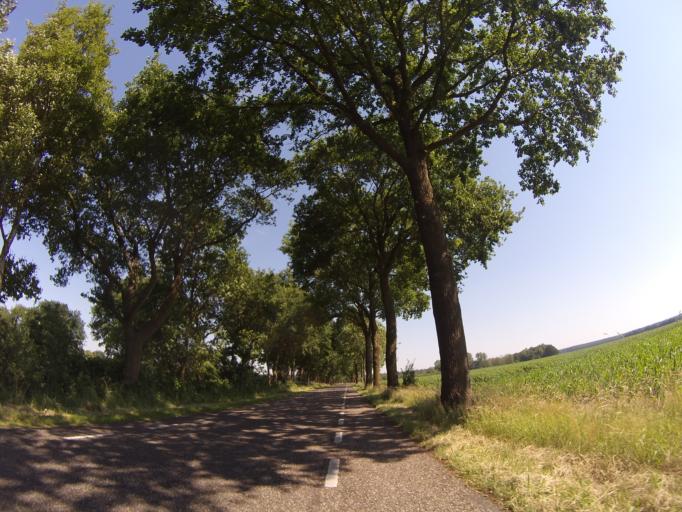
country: NL
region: Drenthe
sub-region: Gemeente Coevorden
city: Sleen
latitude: 52.8099
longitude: 6.7395
